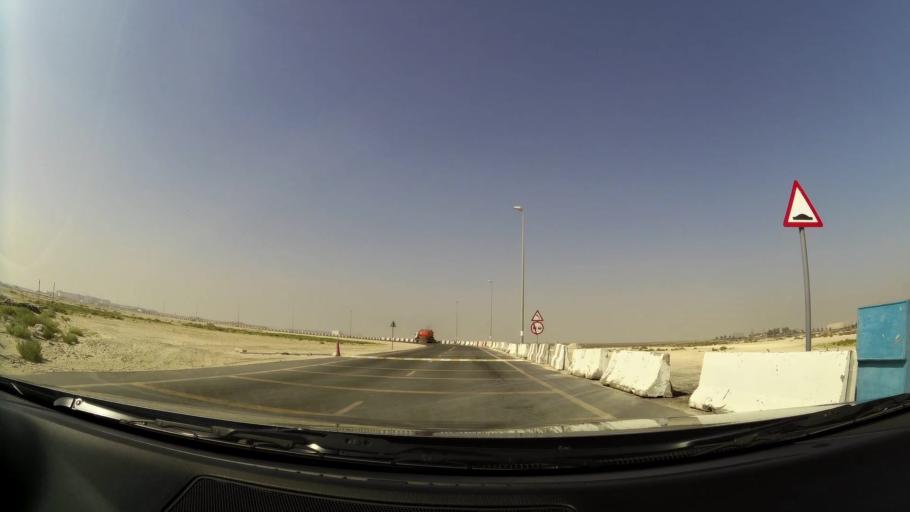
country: AE
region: Dubai
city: Dubai
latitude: 24.9621
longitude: 55.0443
